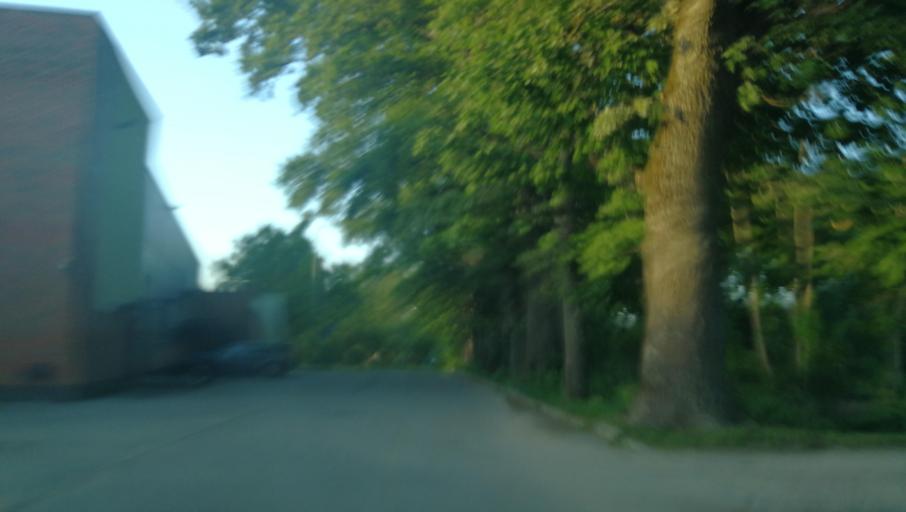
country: LV
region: Cesu Rajons
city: Cesis
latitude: 57.3065
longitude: 25.2534
